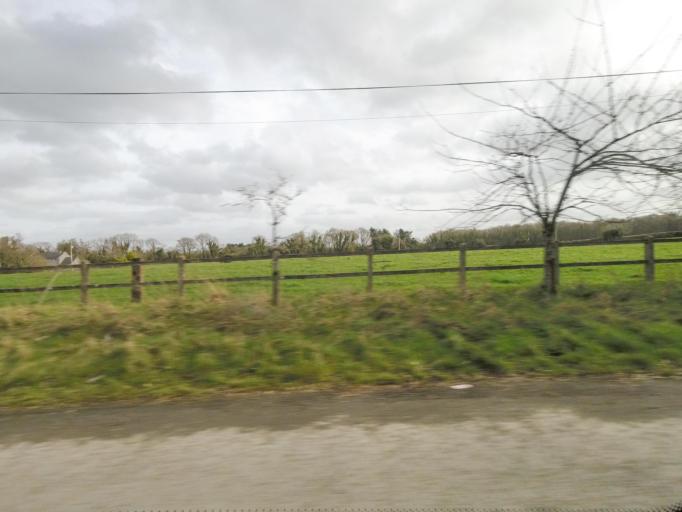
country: IE
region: Leinster
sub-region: Kildare
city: Kilcullen
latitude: 53.1578
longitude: -6.7030
